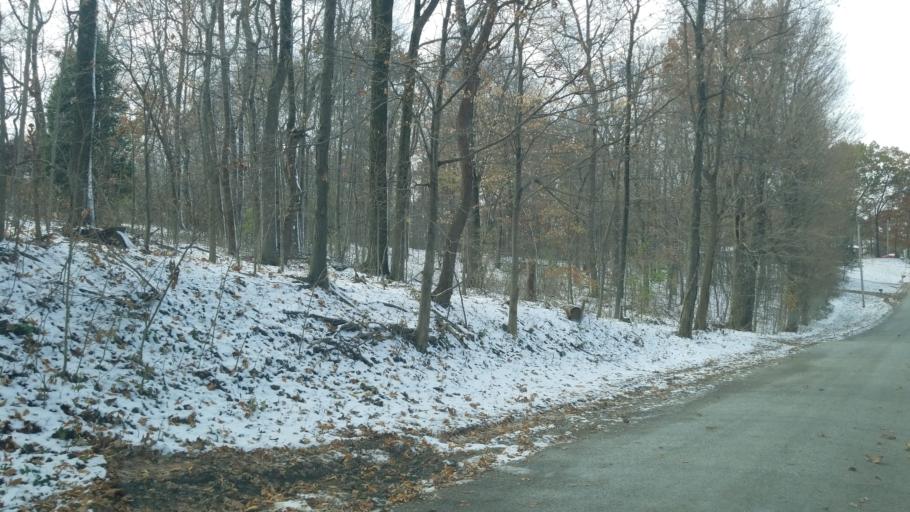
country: US
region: Ohio
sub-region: Licking County
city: Newark
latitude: 40.1462
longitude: -82.3761
